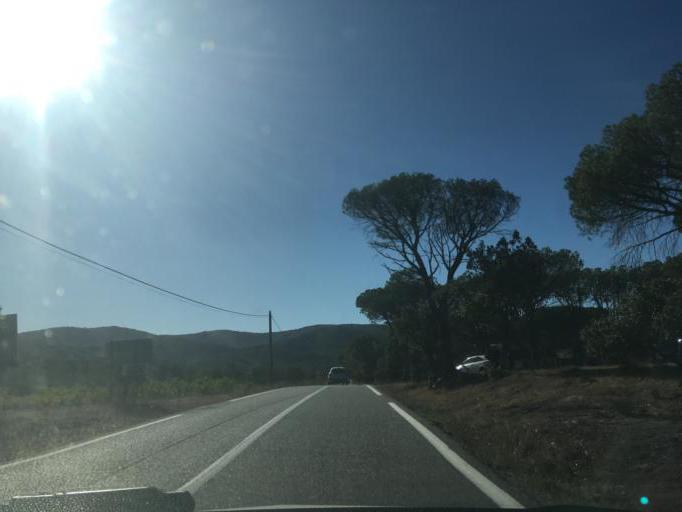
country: FR
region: Provence-Alpes-Cote d'Azur
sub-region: Departement du Var
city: La Garde-Freinet
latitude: 43.3489
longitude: 6.4279
